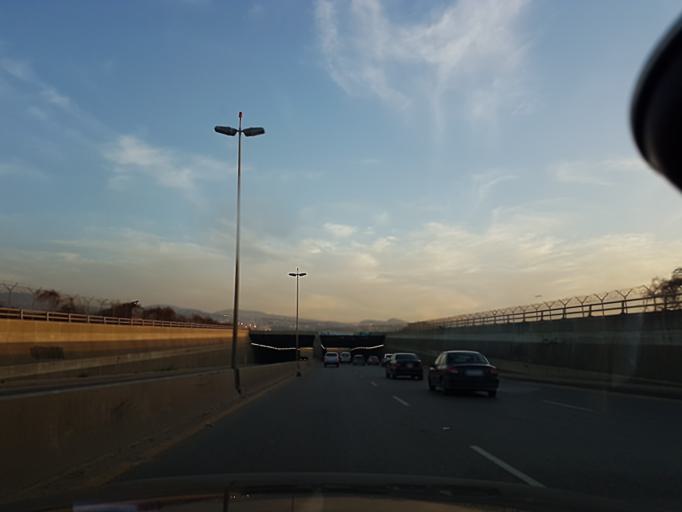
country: LB
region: Mont-Liban
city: Baabda
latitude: 33.8248
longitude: 35.4854
